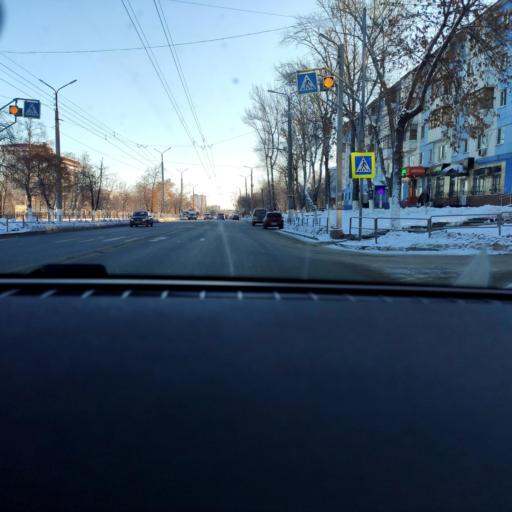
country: RU
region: Samara
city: Novokuybyshevsk
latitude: 53.1000
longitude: 49.9606
